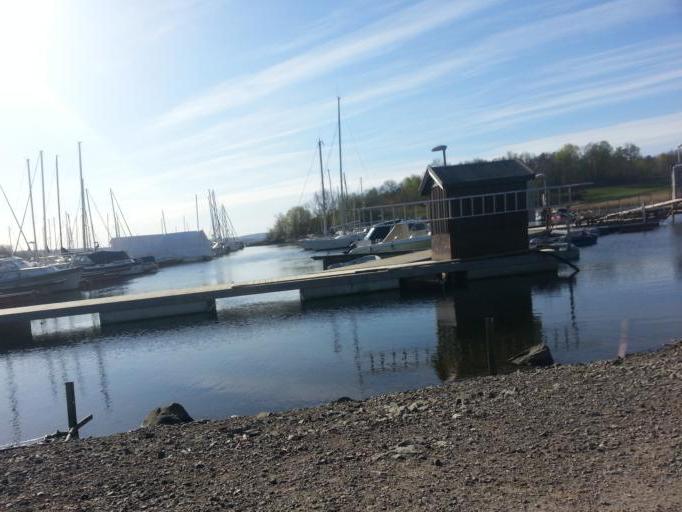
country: NO
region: Oslo
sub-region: Oslo
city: Sjolyststranda
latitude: 59.9174
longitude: 10.6880
